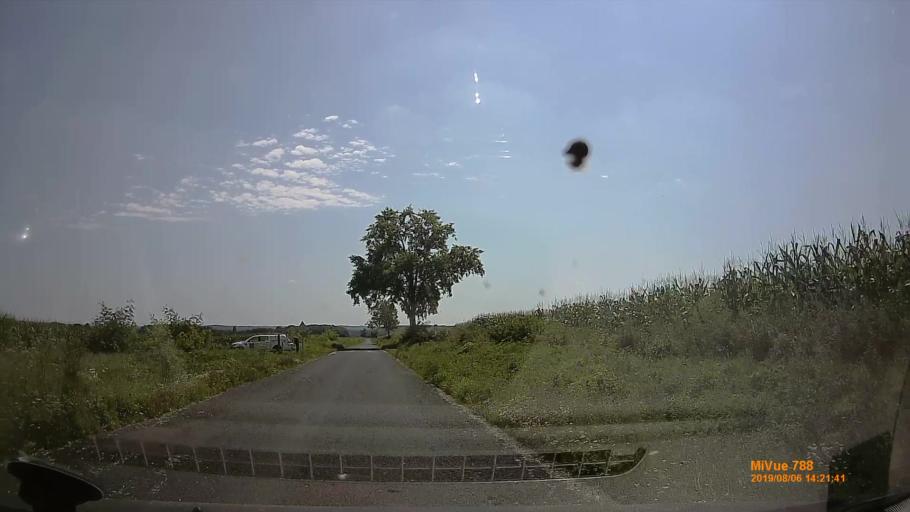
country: HU
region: Zala
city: Zalakomar
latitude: 46.5140
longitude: 17.0839
